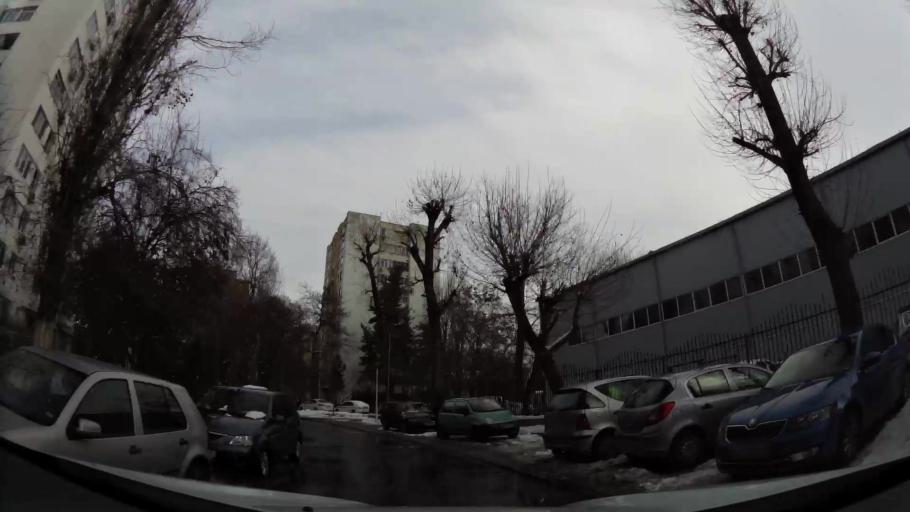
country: RO
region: Ilfov
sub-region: Comuna Popesti-Leordeni
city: Popesti-Leordeni
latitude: 44.3826
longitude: 26.1192
